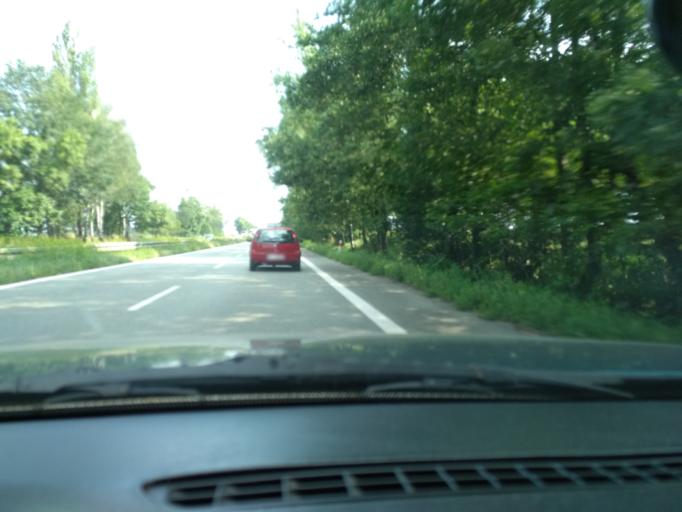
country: PL
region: Silesian Voivodeship
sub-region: Zory
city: Zory
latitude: 50.0071
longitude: 18.7096
